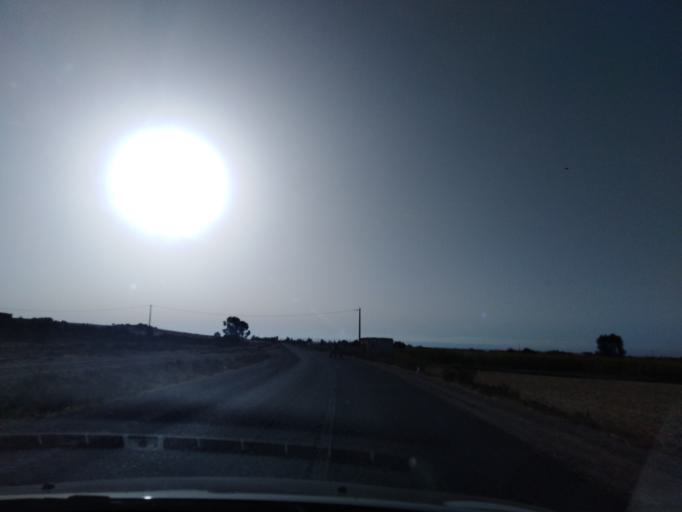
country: MA
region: Doukkala-Abda
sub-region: Safi
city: Safi
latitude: 32.4748
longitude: -8.8704
